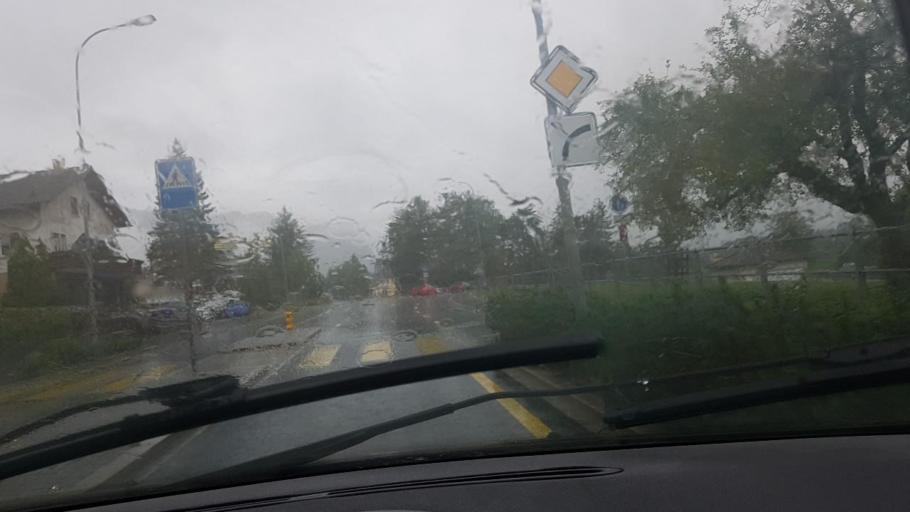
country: LI
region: Balzers
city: Balzers
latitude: 47.0737
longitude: 9.5103
